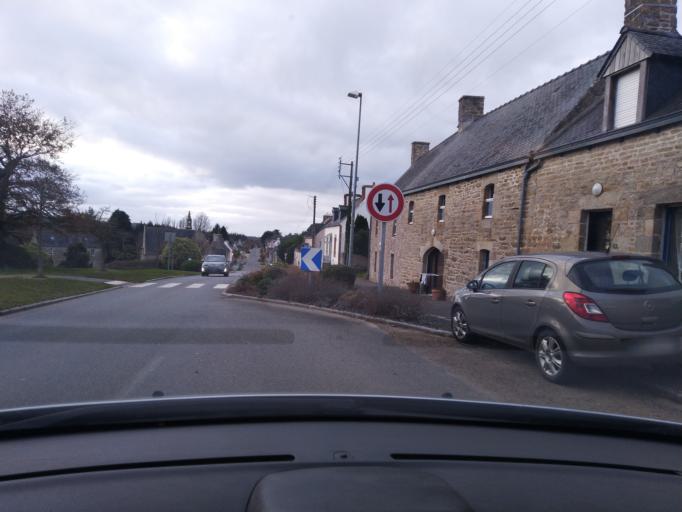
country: FR
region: Brittany
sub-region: Departement du Finistere
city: Guerlesquin
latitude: 48.5661
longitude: -3.5397
